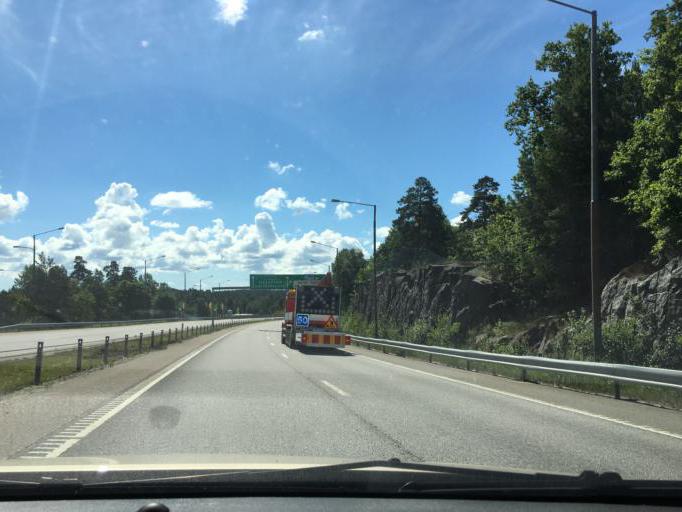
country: SE
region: Stockholm
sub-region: Nacka Kommun
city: Nacka
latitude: 59.3111
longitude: 18.1790
